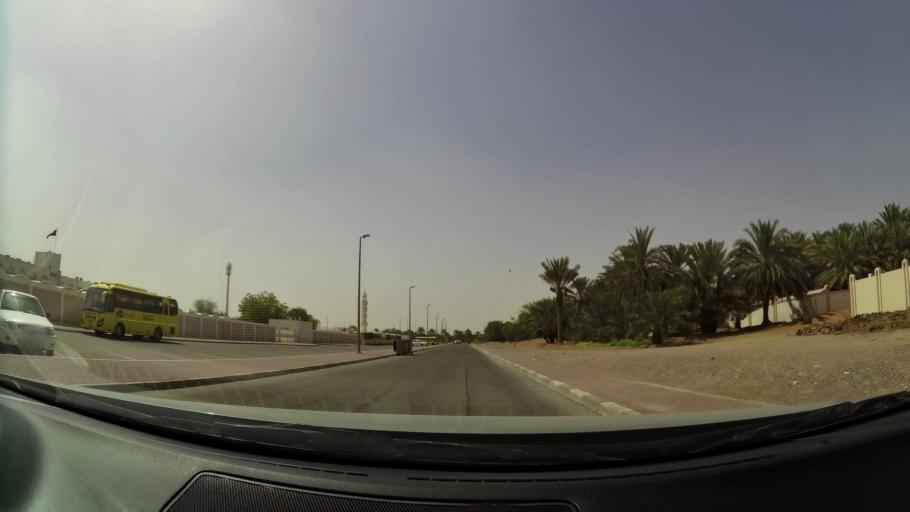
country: AE
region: Abu Dhabi
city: Al Ain
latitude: 24.2301
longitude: 55.7053
